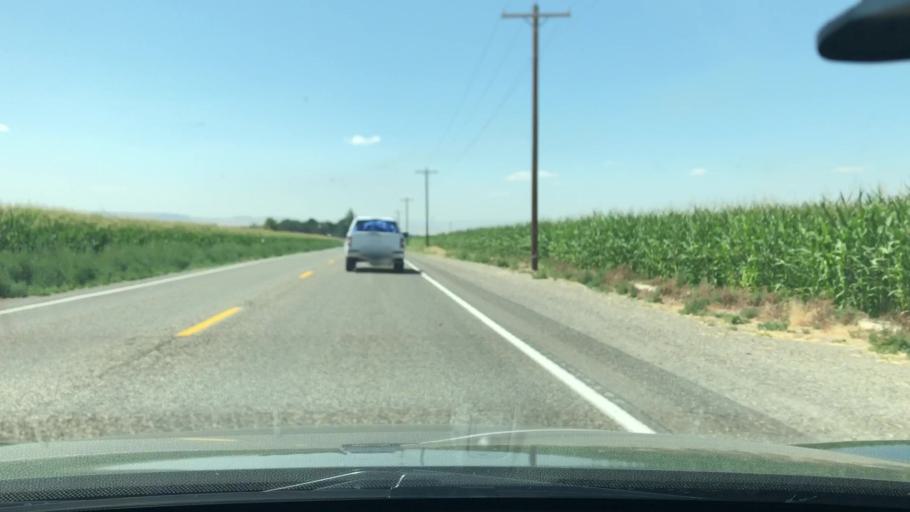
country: US
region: Idaho
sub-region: Owyhee County
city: Marsing
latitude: 43.5453
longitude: -116.8667
